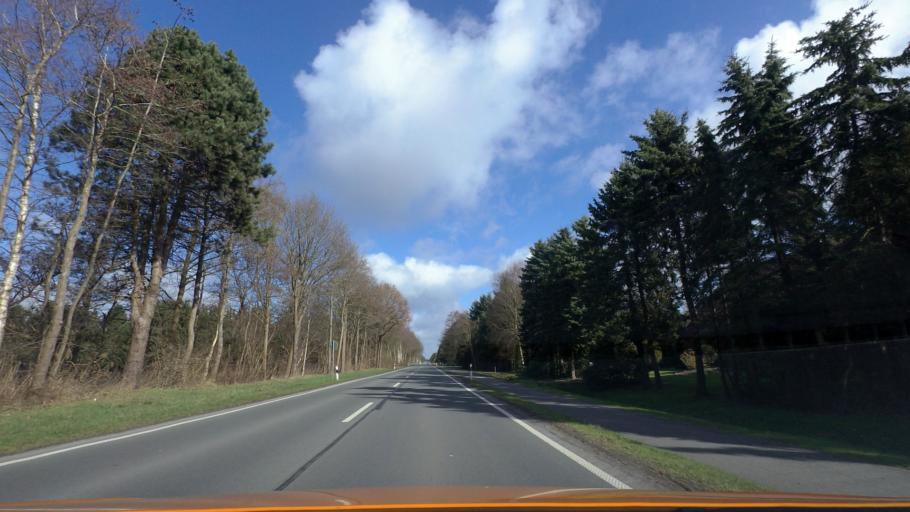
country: DE
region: Lower Saxony
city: Bosel
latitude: 53.0728
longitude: 7.9268
